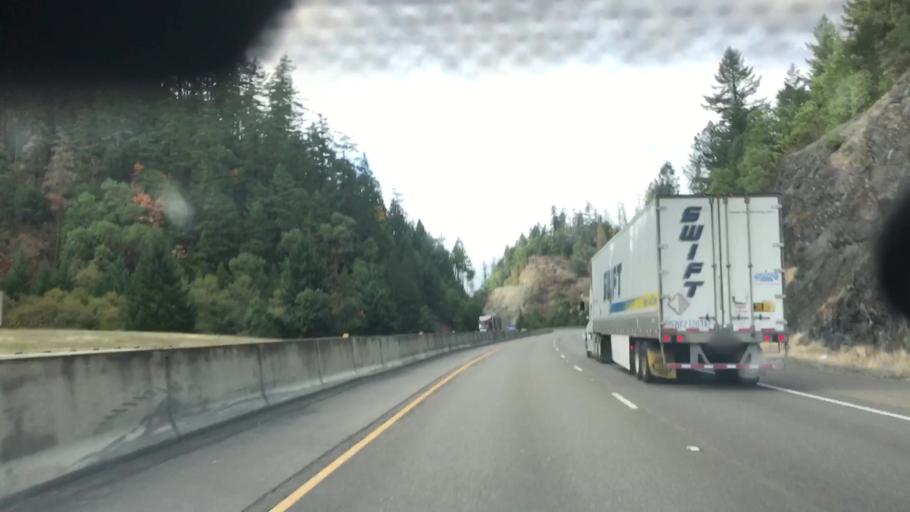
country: US
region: Oregon
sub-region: Douglas County
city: Canyonville
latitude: 42.9102
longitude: -123.2640
